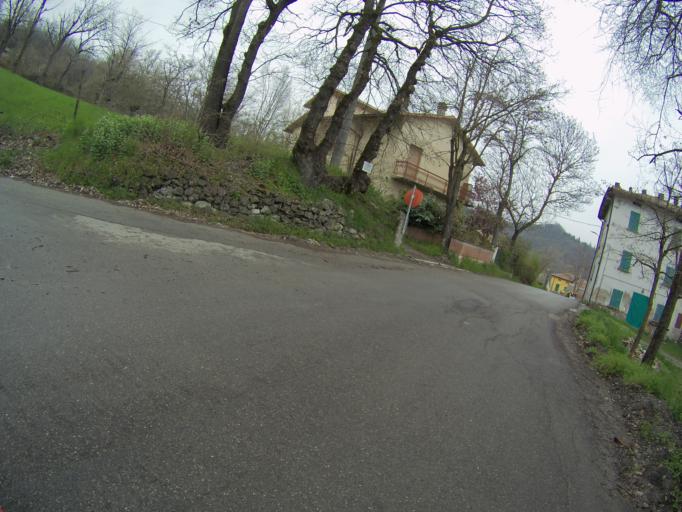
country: IT
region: Emilia-Romagna
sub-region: Provincia di Reggio Emilia
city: Casina
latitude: 44.5361
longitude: 10.4628
